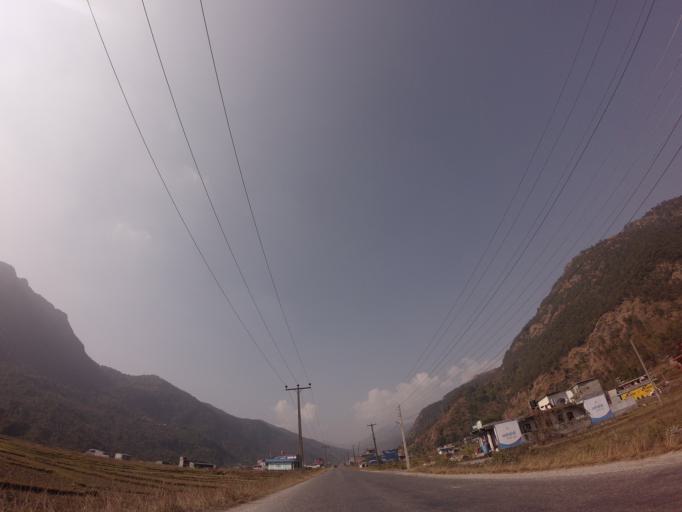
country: NP
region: Western Region
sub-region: Gandaki Zone
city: Pokhara
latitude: 28.2847
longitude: 83.9135
